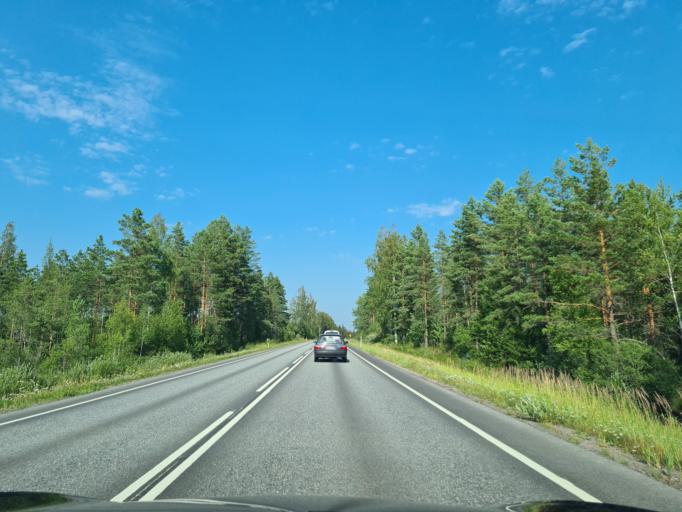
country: FI
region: Satakunta
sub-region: Pori
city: Laengelmaeki
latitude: 61.7662
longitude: 22.1536
